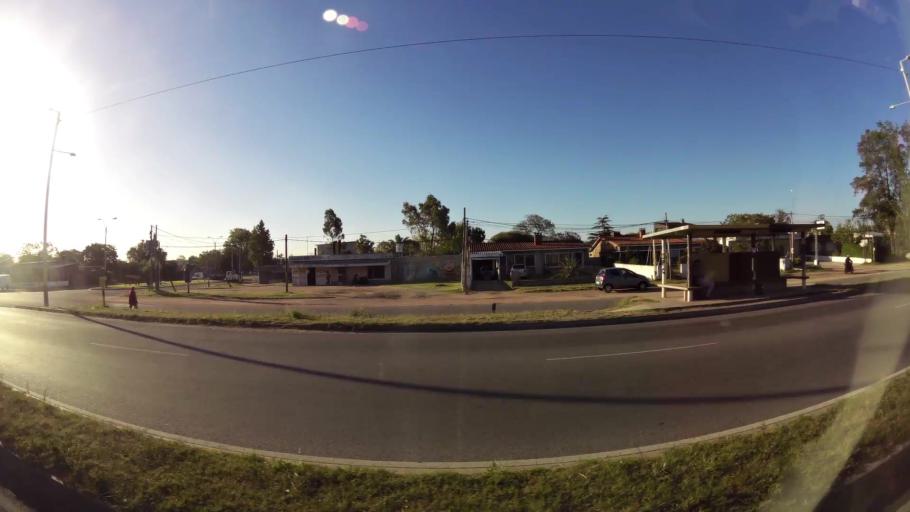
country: UY
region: Canelones
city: Paso de Carrasco
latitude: -34.8583
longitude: -56.0480
